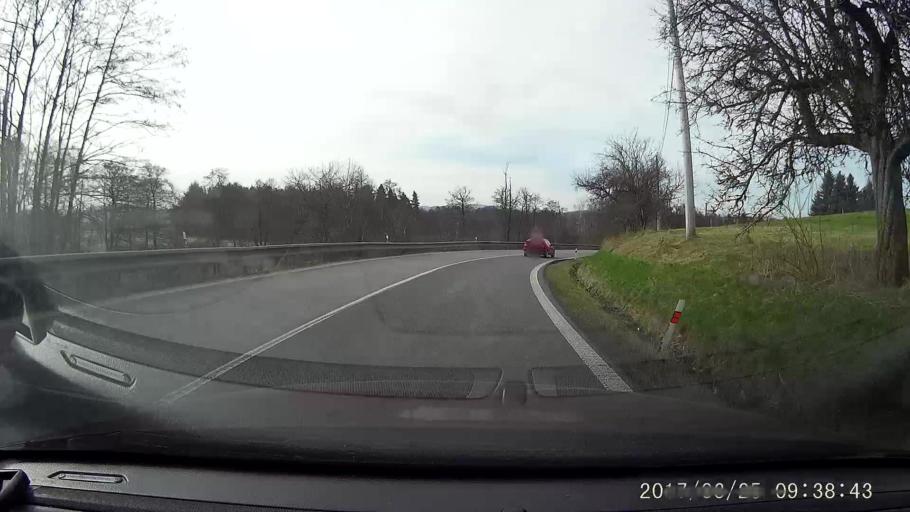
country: CZ
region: Liberecky
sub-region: Okres Liberec
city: Frydlant
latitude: 50.9304
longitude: 15.0948
